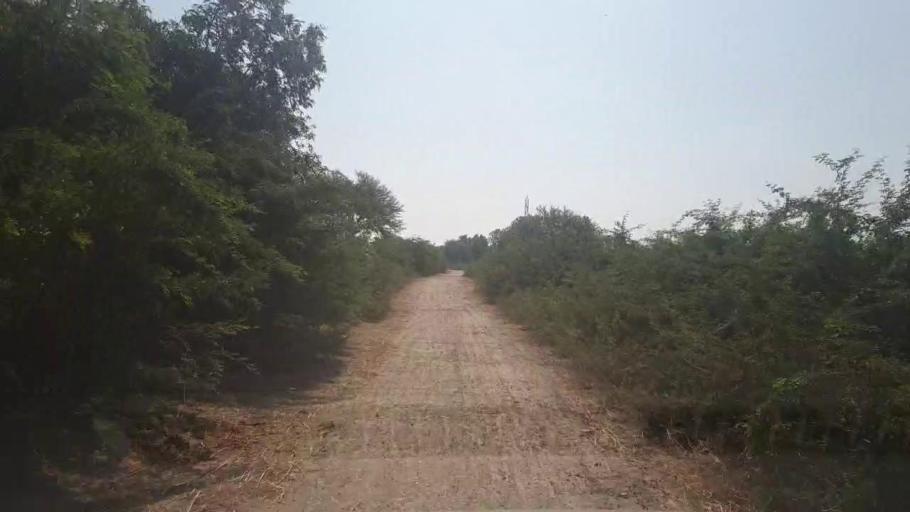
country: PK
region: Sindh
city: Badin
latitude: 24.6786
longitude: 68.8800
